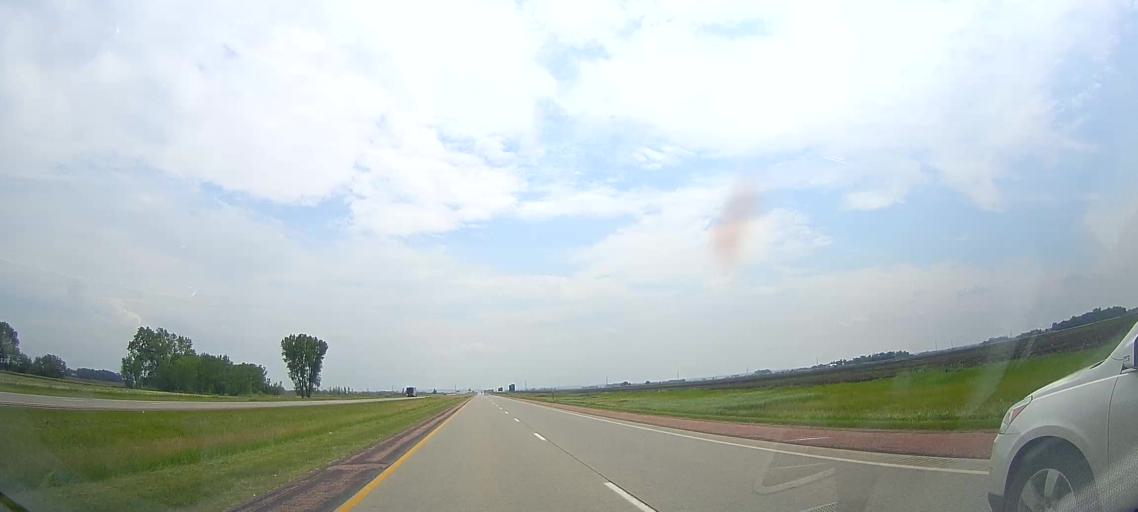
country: US
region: South Dakota
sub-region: Clay County
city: Vermillion
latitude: 42.8096
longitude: -96.7960
